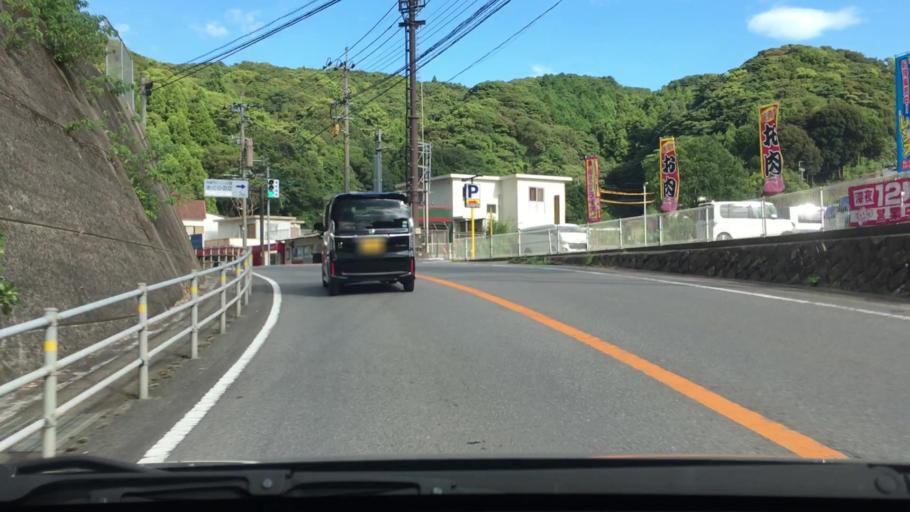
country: JP
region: Nagasaki
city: Togitsu
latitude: 32.8083
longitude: 129.8130
